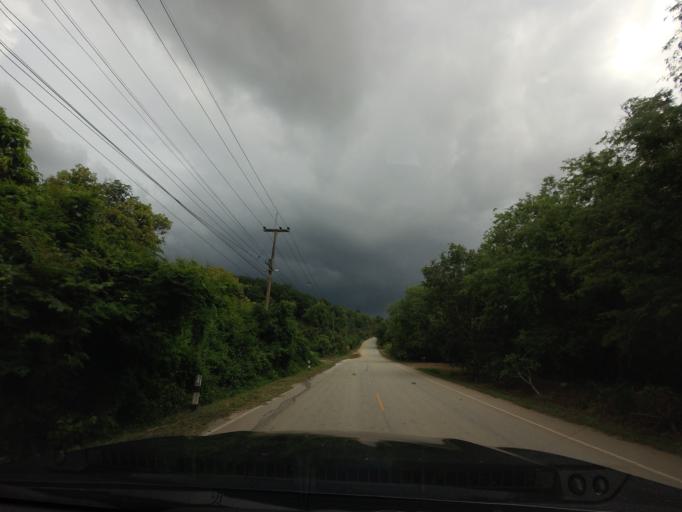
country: LA
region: Vientiane
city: Muang Sanakham
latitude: 17.9689
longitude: 101.7469
